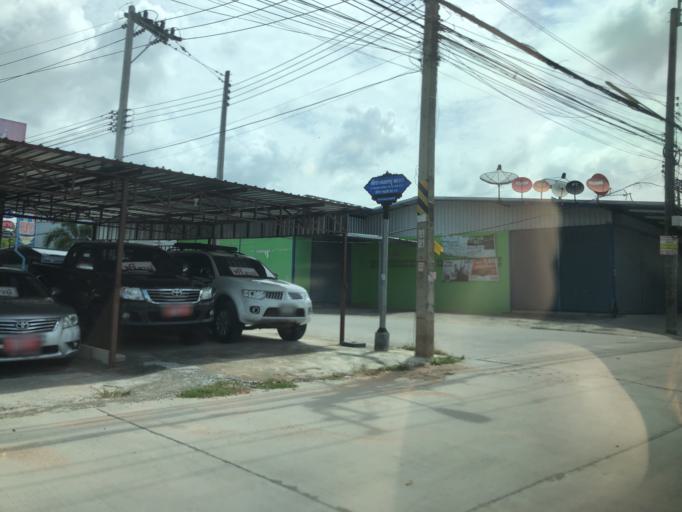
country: TH
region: Chon Buri
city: Si Racha
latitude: 13.1499
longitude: 100.9724
